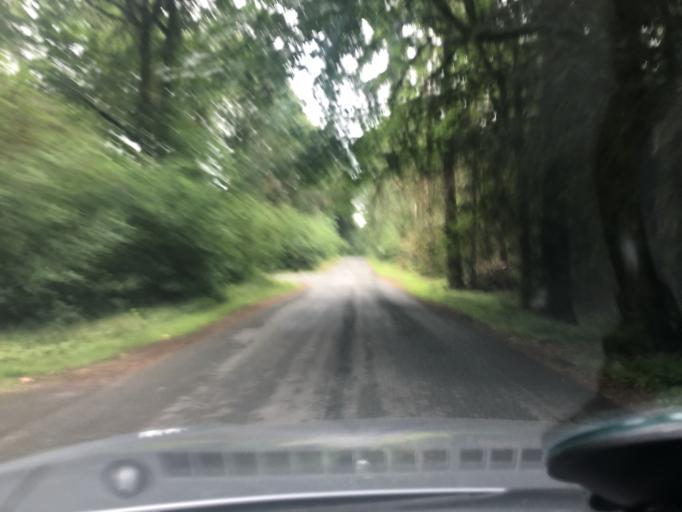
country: US
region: Washington
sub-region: King County
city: Black Diamond
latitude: 47.3224
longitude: -122.0362
